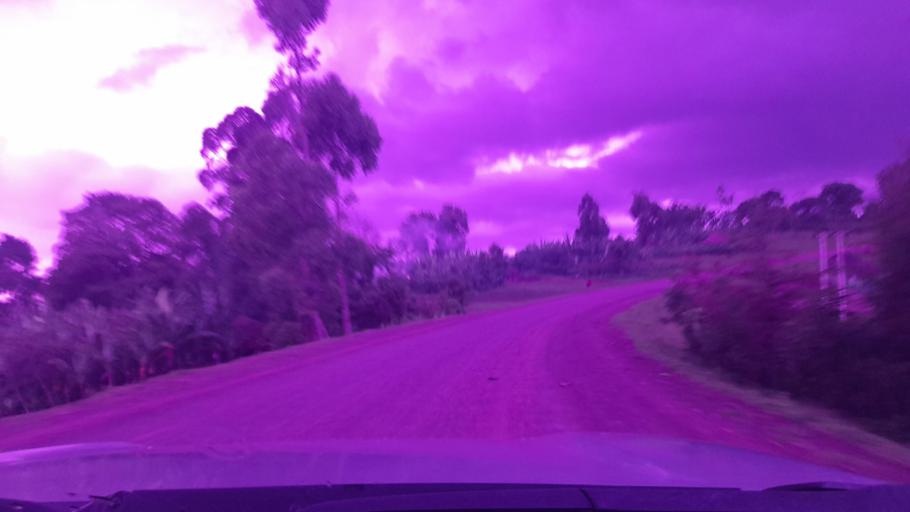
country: ET
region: Southern Nations, Nationalities, and People's Region
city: Mizan Teferi
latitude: 6.9016
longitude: 35.8392
